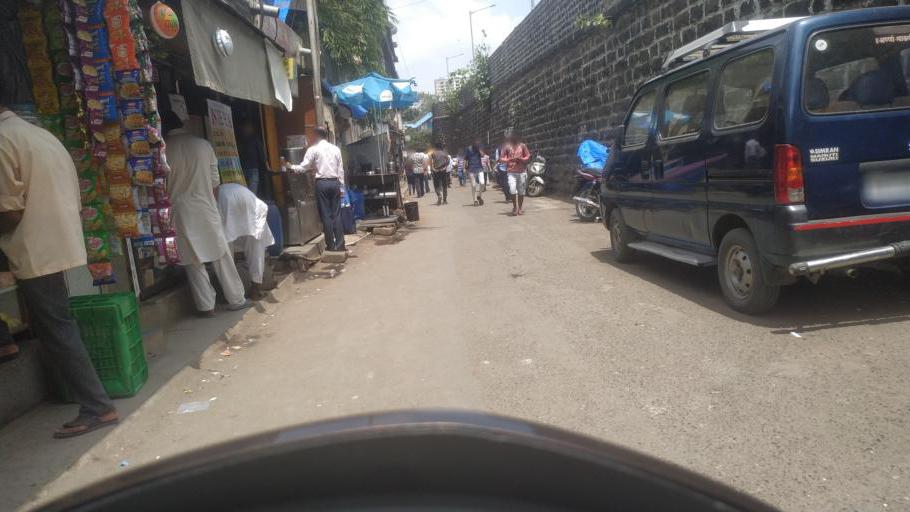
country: IN
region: Maharashtra
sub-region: Mumbai Suburban
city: Mumbai
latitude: 19.0083
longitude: 72.8350
